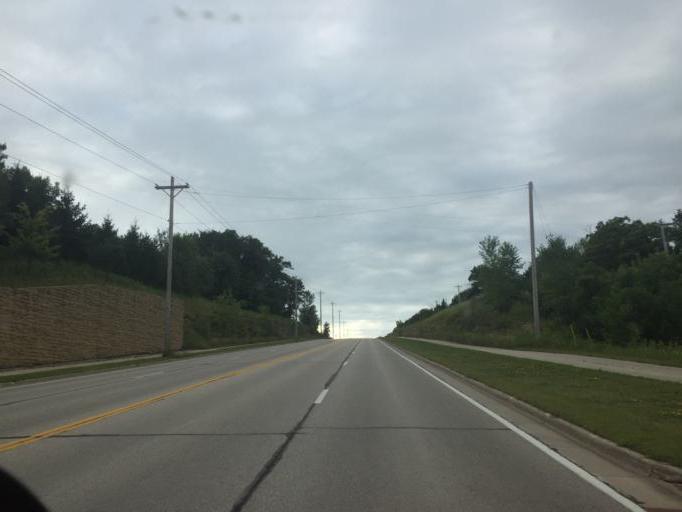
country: US
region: Minnesota
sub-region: Olmsted County
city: Rochester
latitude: 43.9640
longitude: -92.4812
